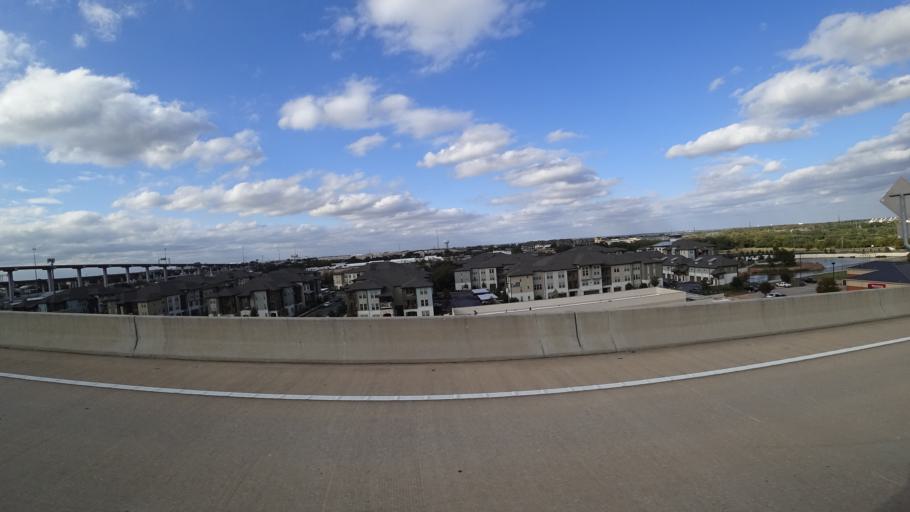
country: US
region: Texas
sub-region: Williamson County
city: Anderson Mill
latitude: 30.4700
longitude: -97.7931
